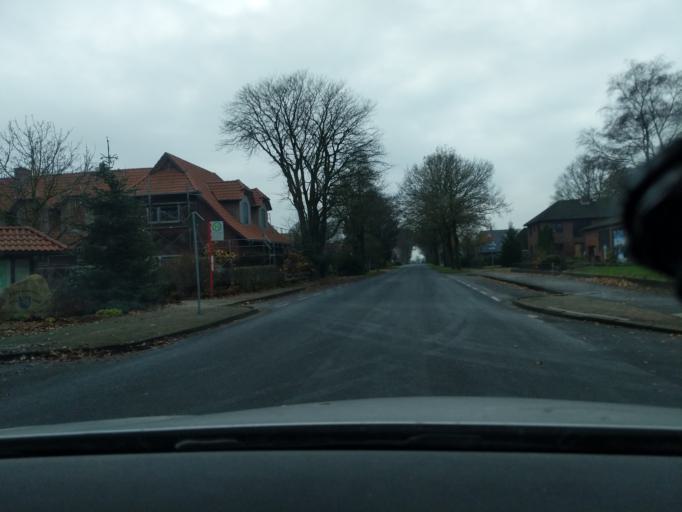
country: DE
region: Lower Saxony
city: Ahlerstedt
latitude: 53.3964
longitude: 9.4882
